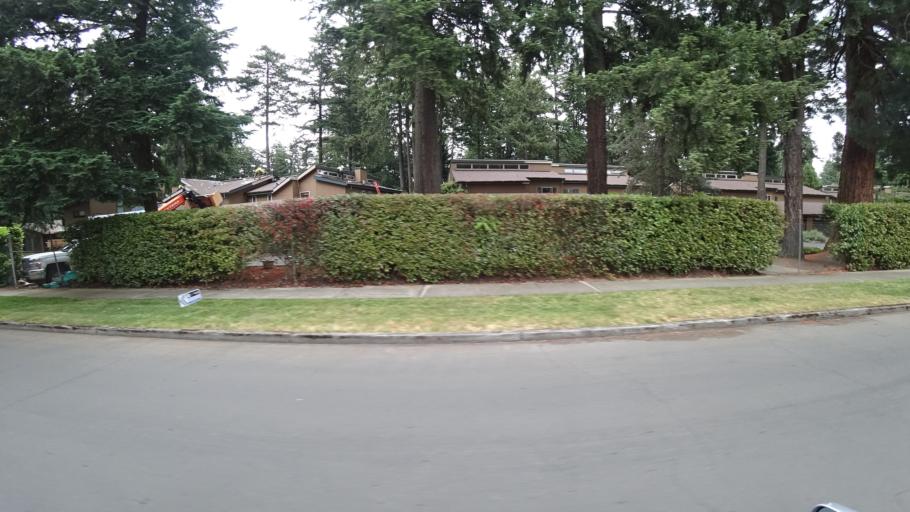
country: US
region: Oregon
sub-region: Clackamas County
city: Happy Valley
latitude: 45.4994
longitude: -122.5060
